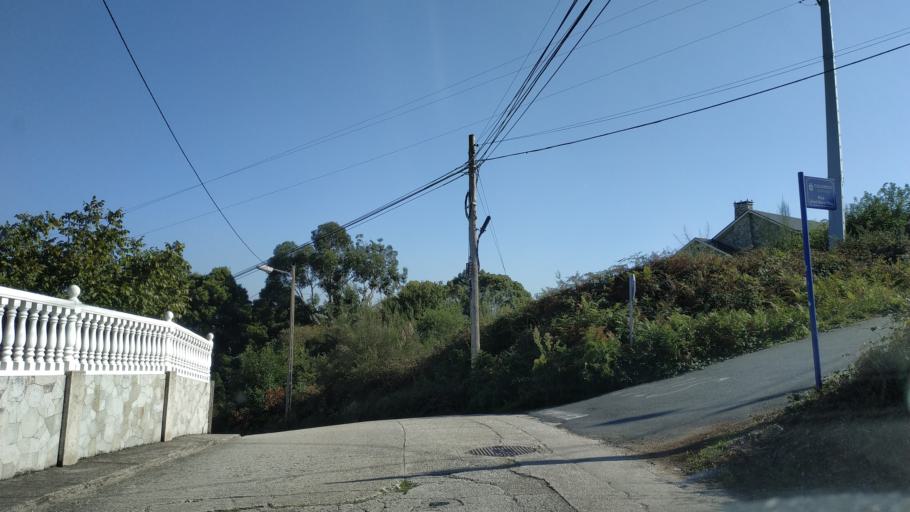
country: ES
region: Galicia
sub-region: Provincia da Coruna
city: Culleredo
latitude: 43.3233
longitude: -8.3861
